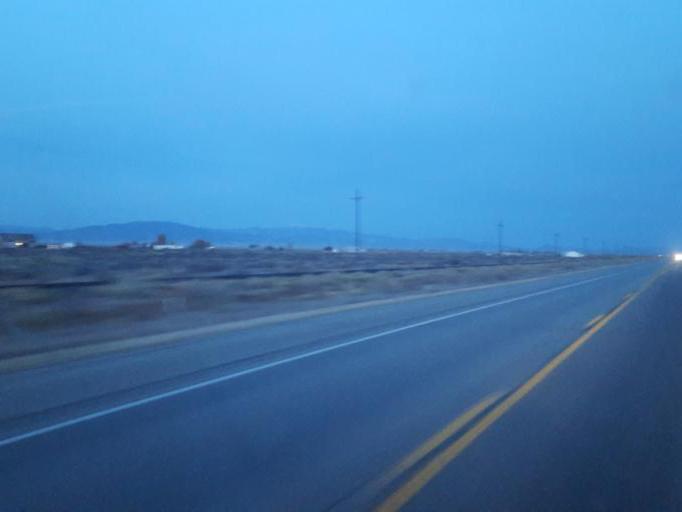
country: US
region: Colorado
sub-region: Alamosa County
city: Alamosa
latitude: 37.5026
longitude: -105.9592
